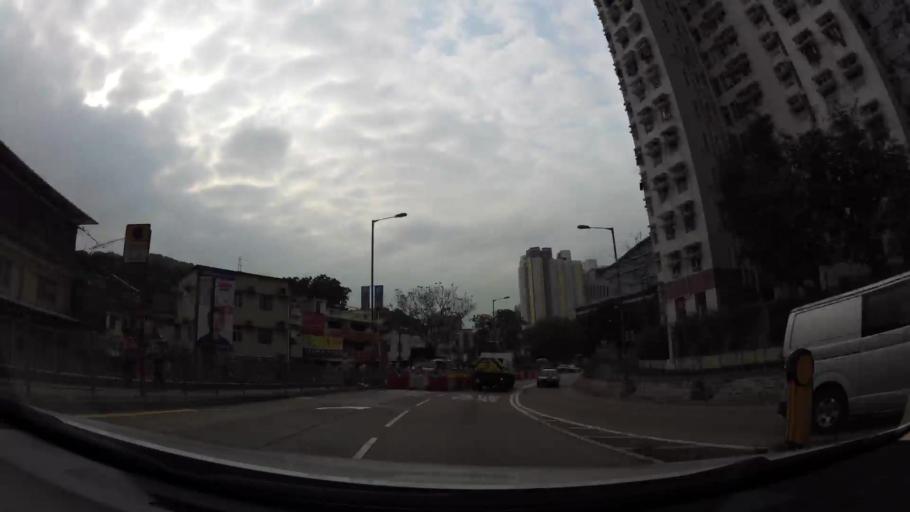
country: HK
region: Tai Po
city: Tai Po
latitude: 22.4443
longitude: 114.1669
